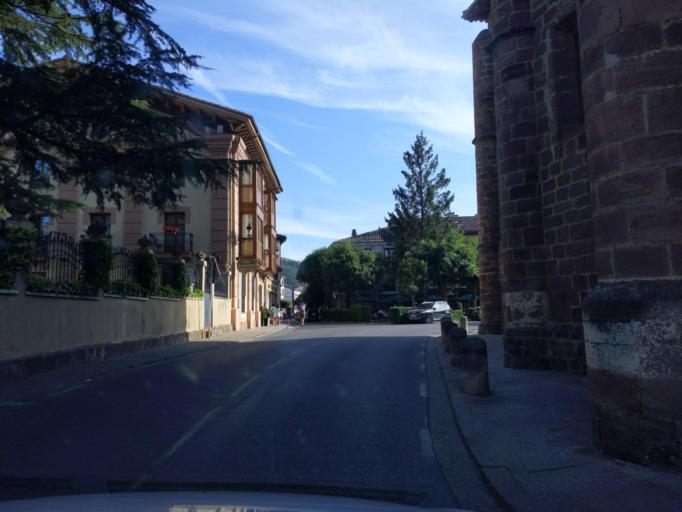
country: ES
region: La Rioja
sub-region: Provincia de La Rioja
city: Ezcaray
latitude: 42.3262
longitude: -3.0143
